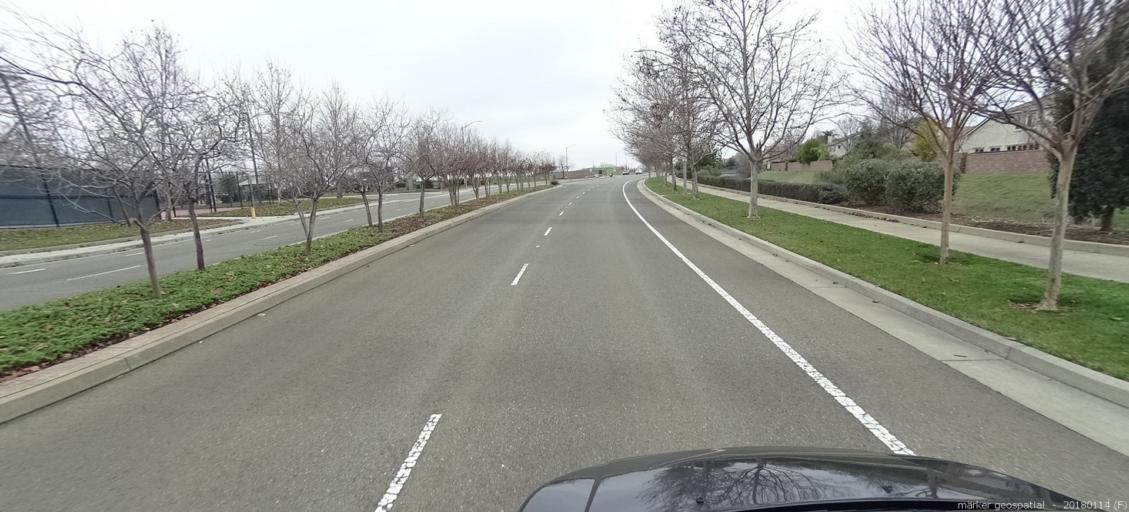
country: US
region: California
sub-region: Sacramento County
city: Rancho Cordova
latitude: 38.5486
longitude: -121.2367
